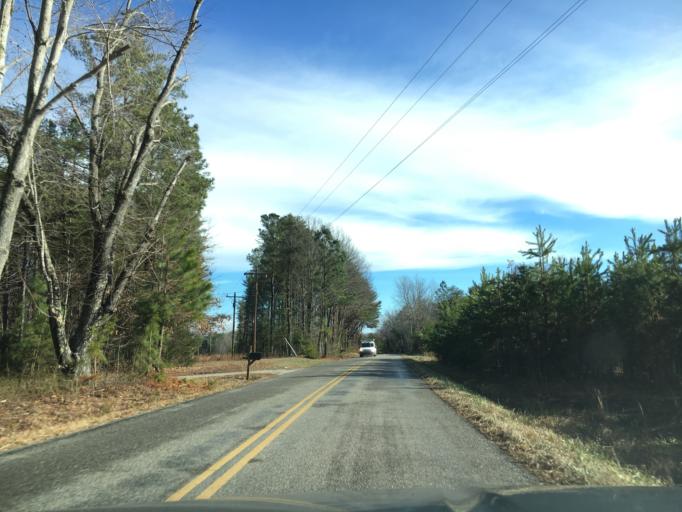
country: US
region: Virginia
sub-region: Amelia County
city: Amelia Court House
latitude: 37.3935
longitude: -78.1089
